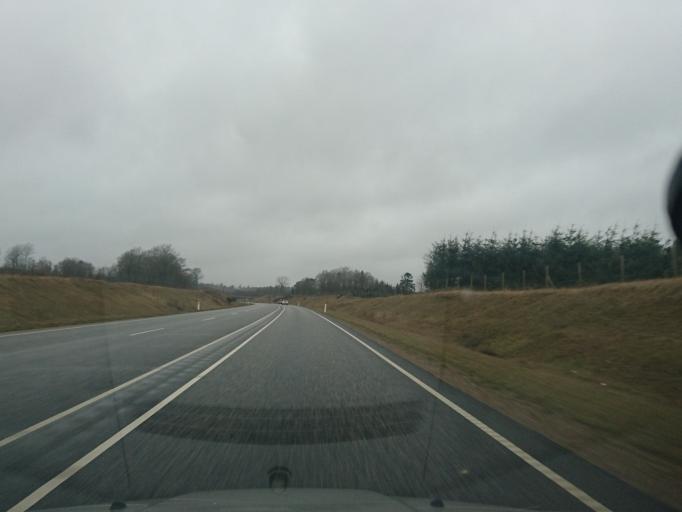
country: DK
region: South Denmark
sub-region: Vejle Kommune
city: Egtved
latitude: 55.7034
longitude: 9.2943
